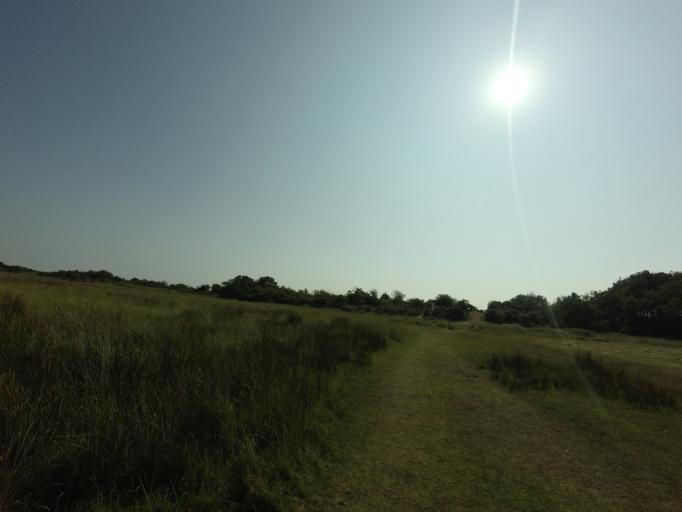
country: NL
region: Friesland
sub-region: Gemeente Schiermonnikoog
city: Schiermonnikoog
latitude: 53.4882
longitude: 6.2228
